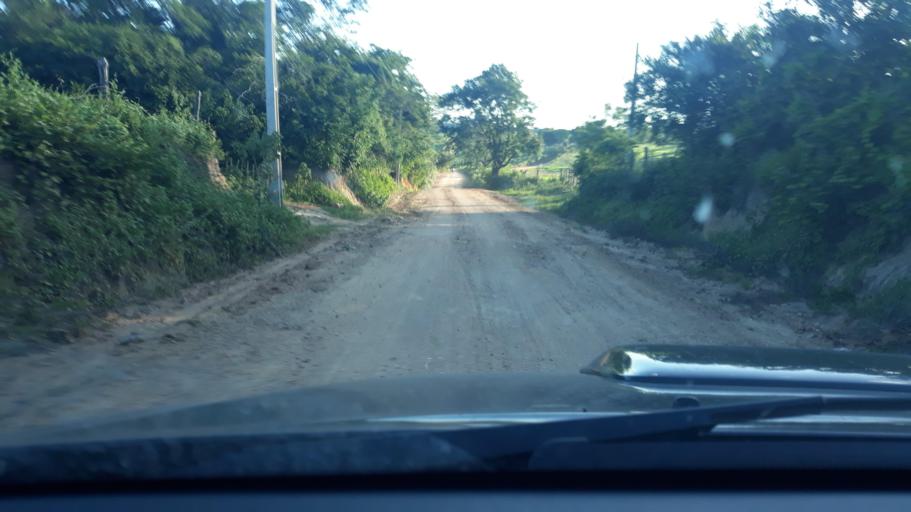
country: BR
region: Bahia
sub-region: Riacho De Santana
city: Riacho de Santana
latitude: -13.8213
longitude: -42.7245
